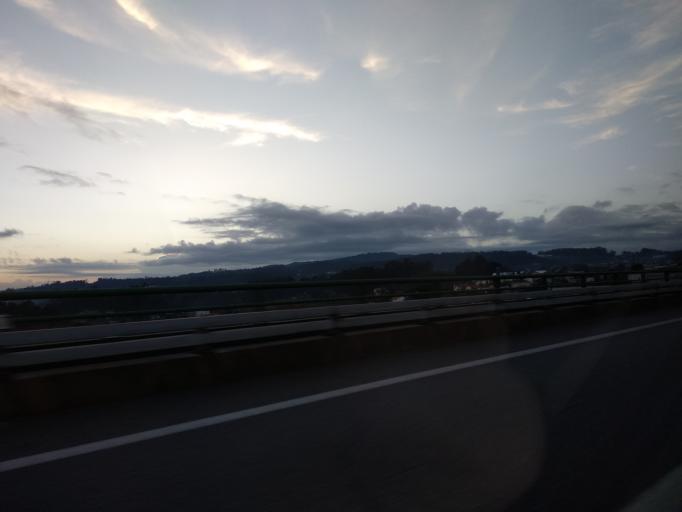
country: PT
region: Braga
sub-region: Braga
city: Oliveira
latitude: 41.5004
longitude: -8.4716
